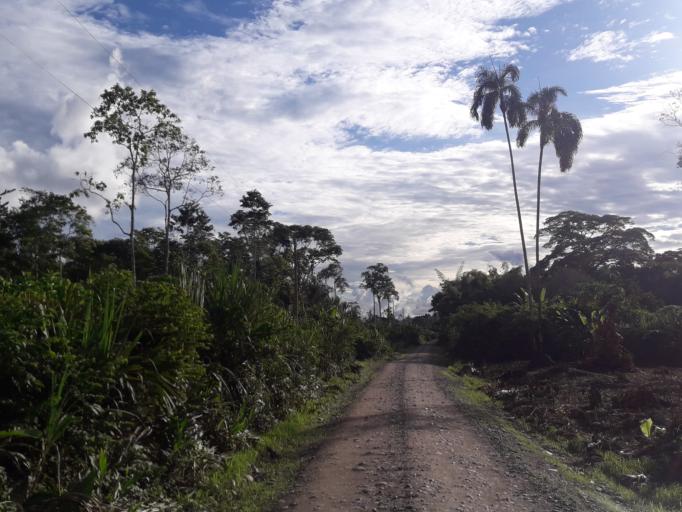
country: EC
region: Orellana
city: Boca Suno
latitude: -0.8833
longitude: -77.2885
